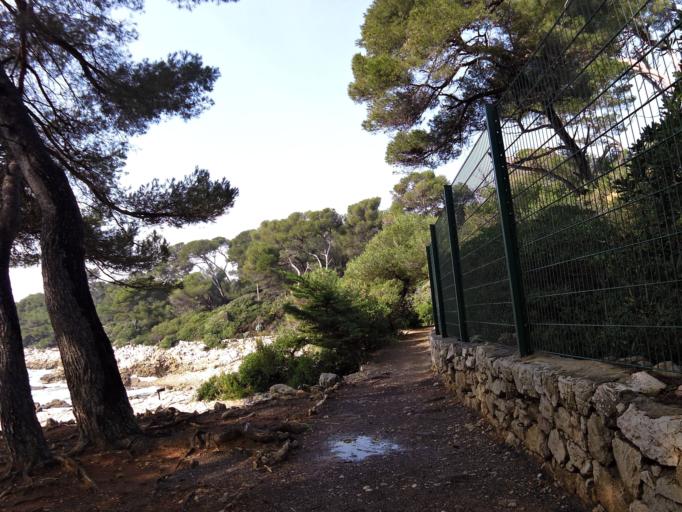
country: FR
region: Provence-Alpes-Cote d'Azur
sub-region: Departement des Alpes-Maritimes
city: Antibes
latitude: 43.5447
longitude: 7.1327
